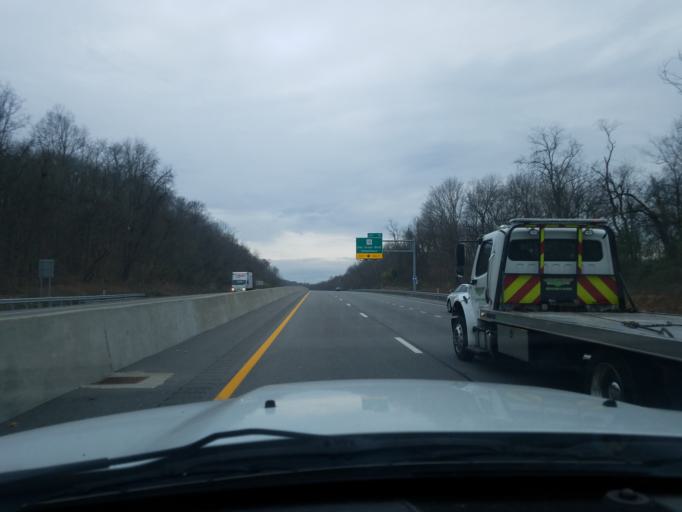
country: US
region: West Virginia
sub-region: Cabell County
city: Huntington
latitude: 38.3982
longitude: -82.3934
